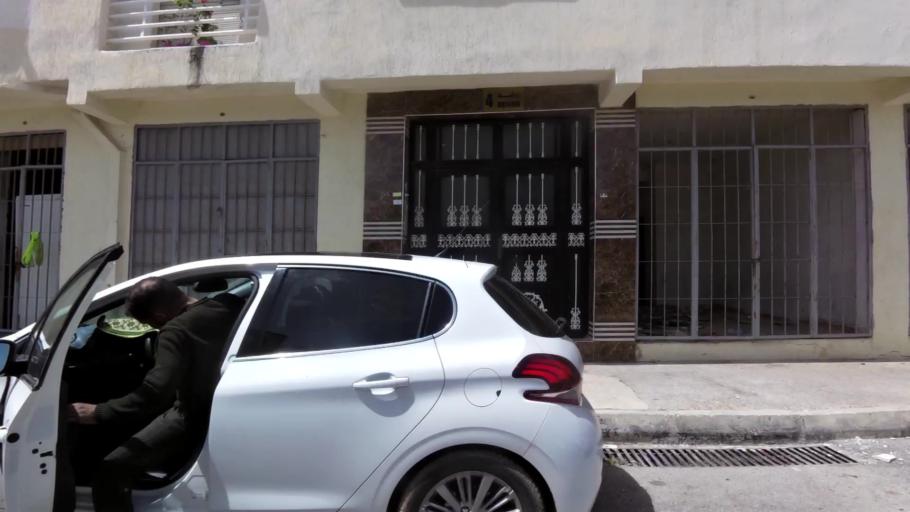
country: MA
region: Tanger-Tetouan
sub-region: Tanger-Assilah
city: Tangier
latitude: 35.7462
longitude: -5.8472
